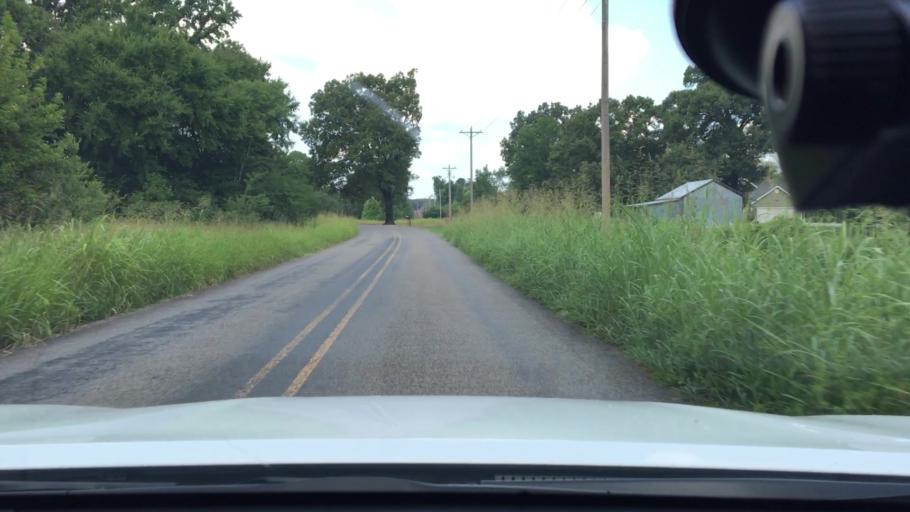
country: US
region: Arkansas
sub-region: Logan County
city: Paris
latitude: 35.2691
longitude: -93.6629
